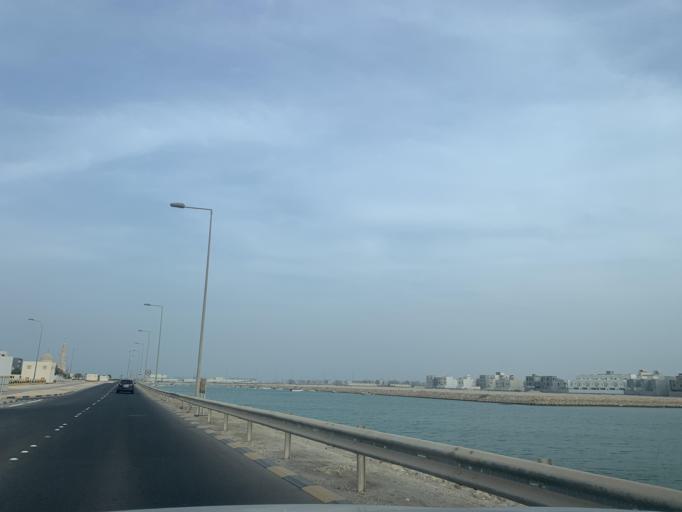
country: BH
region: Muharraq
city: Al Muharraq
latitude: 26.2979
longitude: 50.6362
